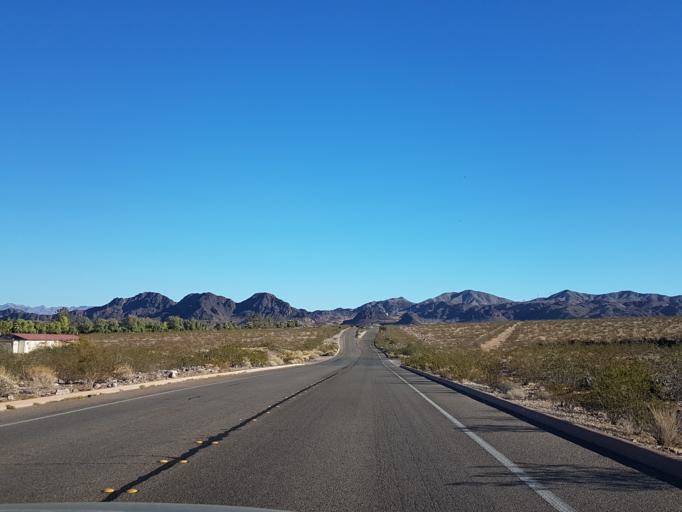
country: US
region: Nevada
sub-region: Clark County
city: Boulder City
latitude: 36.0404
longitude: -114.8079
